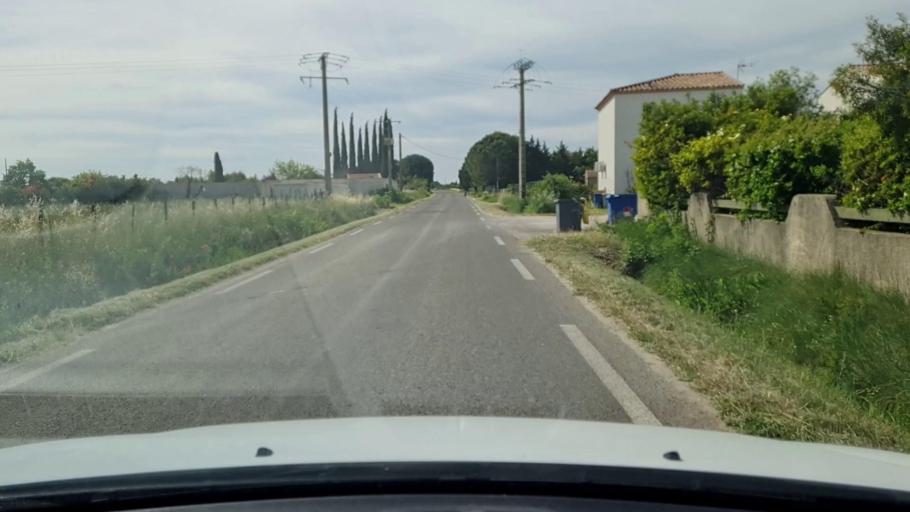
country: FR
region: Languedoc-Roussillon
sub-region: Departement de l'Herault
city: Marsillargues
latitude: 43.6277
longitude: 4.1978
